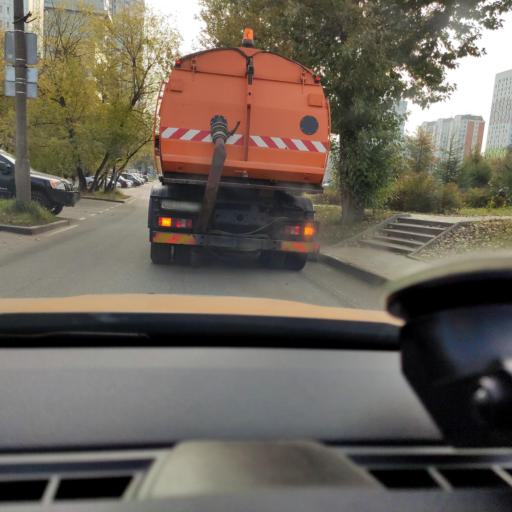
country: RU
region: Moskovskaya
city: Bol'shaya Setun'
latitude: 55.7427
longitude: 37.4135
